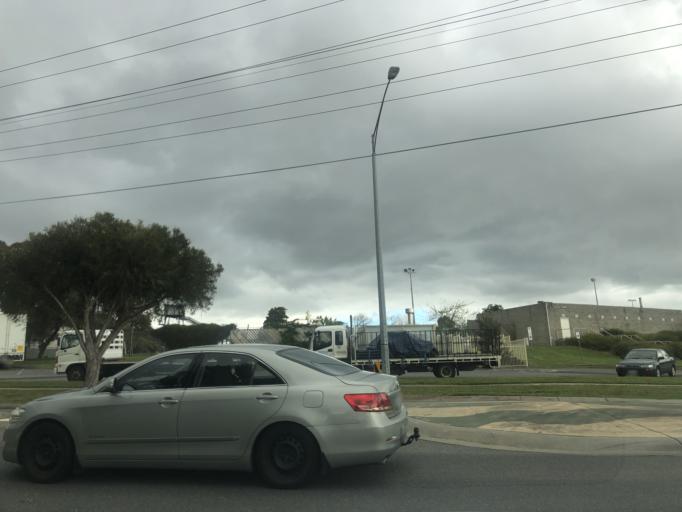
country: AU
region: Victoria
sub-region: Casey
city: Doveton
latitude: -37.9876
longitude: 145.2441
